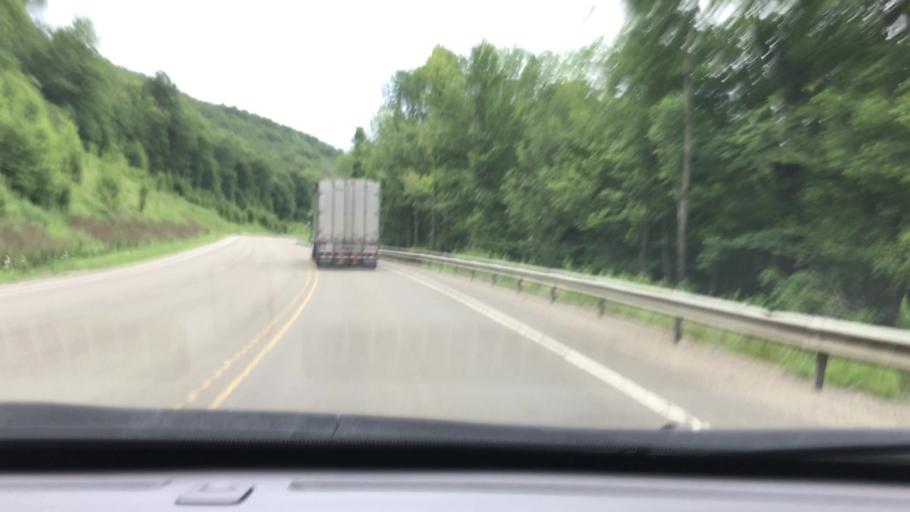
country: US
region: Pennsylvania
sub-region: McKean County
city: Kane
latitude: 41.7522
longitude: -78.6924
